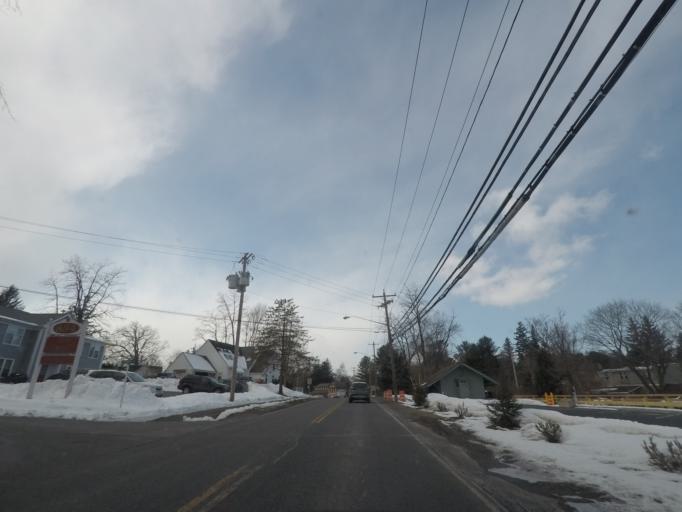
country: US
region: New York
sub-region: Albany County
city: Delmar
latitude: 42.6290
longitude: -73.8630
